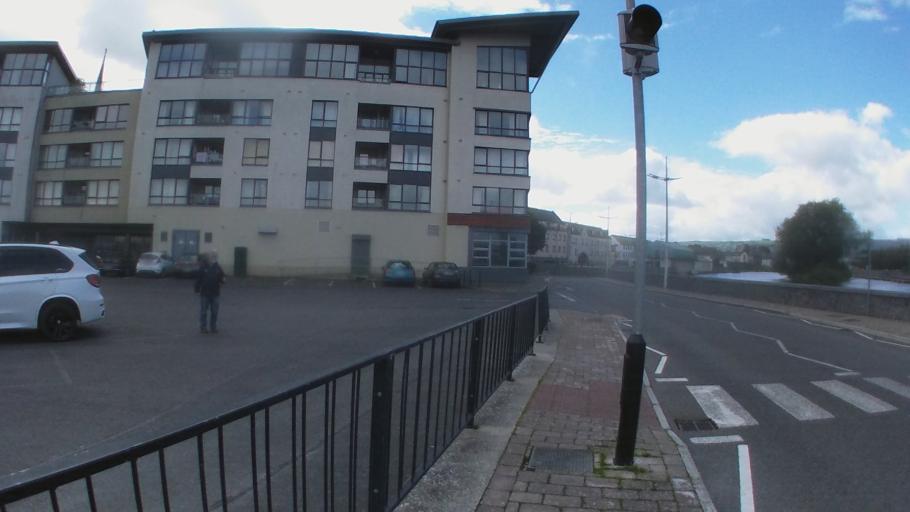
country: IE
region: Leinster
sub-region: County Carlow
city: Carlow
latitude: 52.8381
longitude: -6.9339
